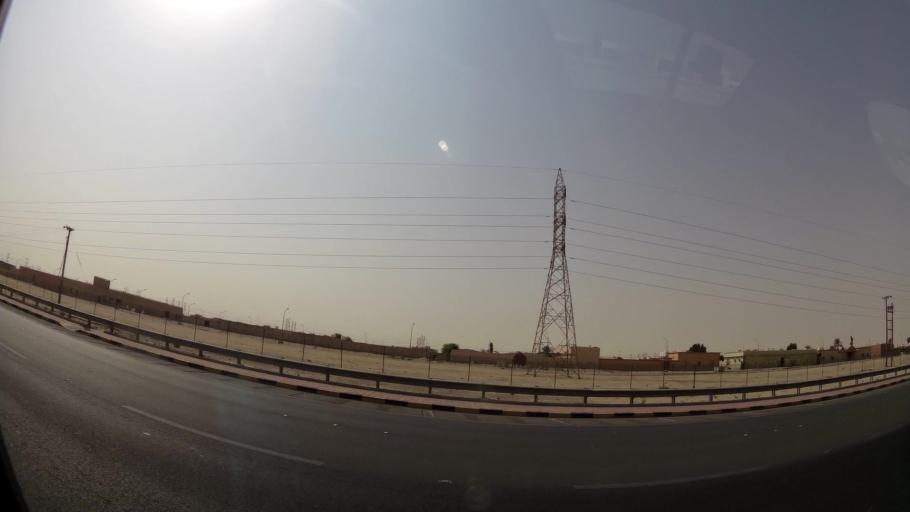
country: KW
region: Muhafazat al Jahra'
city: Al Jahra'
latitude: 29.3092
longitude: 47.6593
